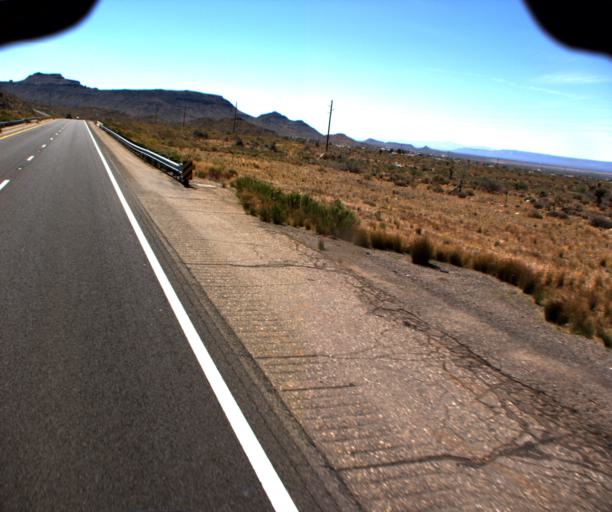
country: US
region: Arizona
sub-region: Mohave County
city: Golden Valley
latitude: 35.2494
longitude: -114.1527
